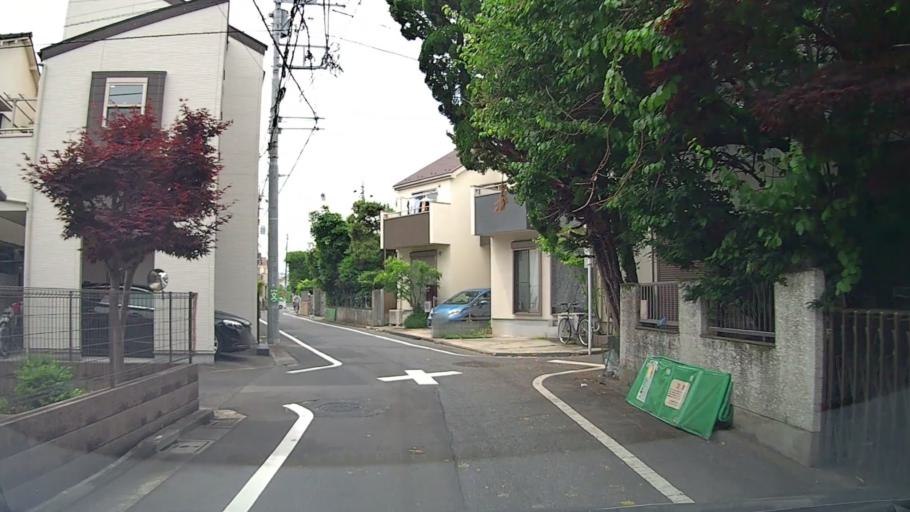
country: JP
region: Tokyo
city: Musashino
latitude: 35.7148
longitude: 139.6225
